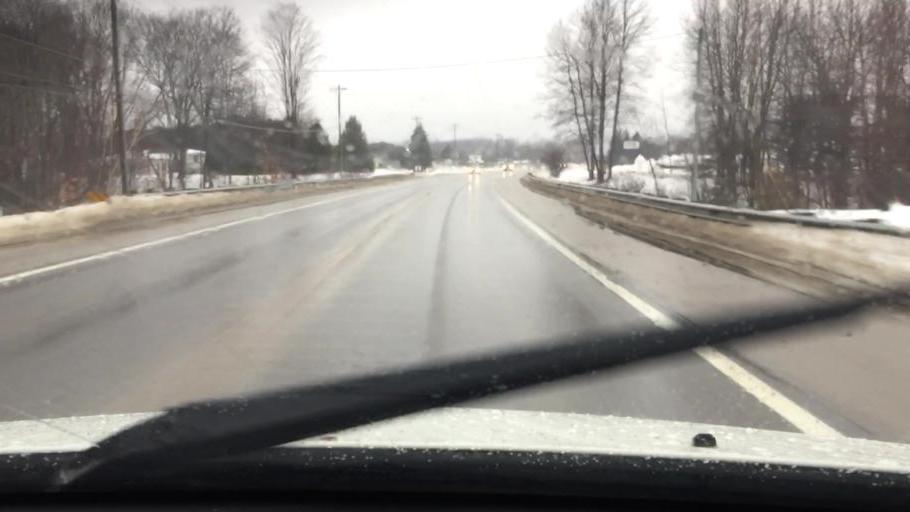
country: US
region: Michigan
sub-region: Charlevoix County
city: Charlevoix
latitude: 45.2952
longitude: -85.2531
